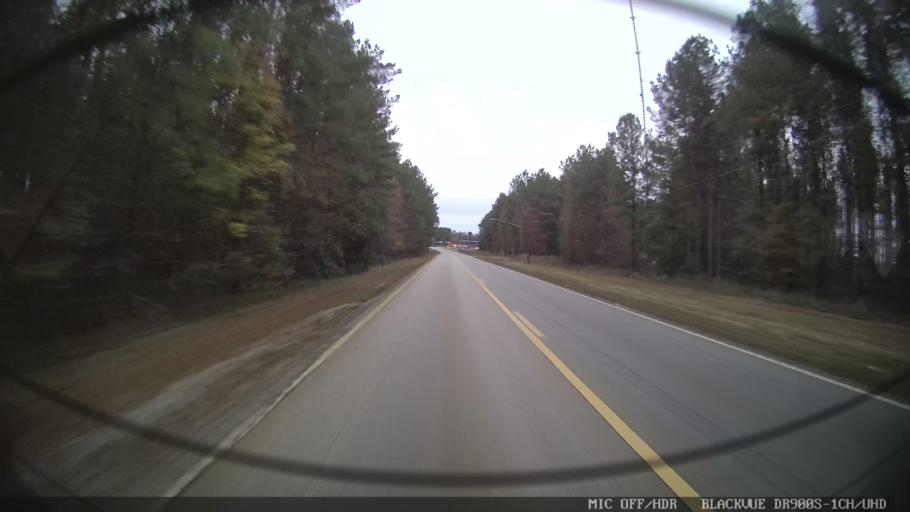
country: US
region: Mississippi
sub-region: Clarke County
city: Stonewall
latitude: 32.0549
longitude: -88.8990
